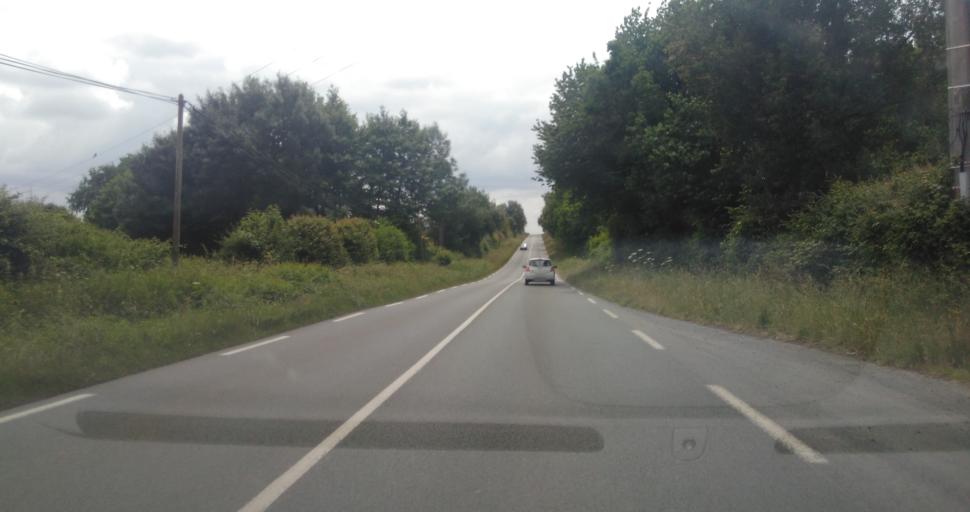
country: FR
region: Pays de la Loire
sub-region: Departement de la Vendee
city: Bournezeau
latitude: 46.6257
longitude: -1.1597
